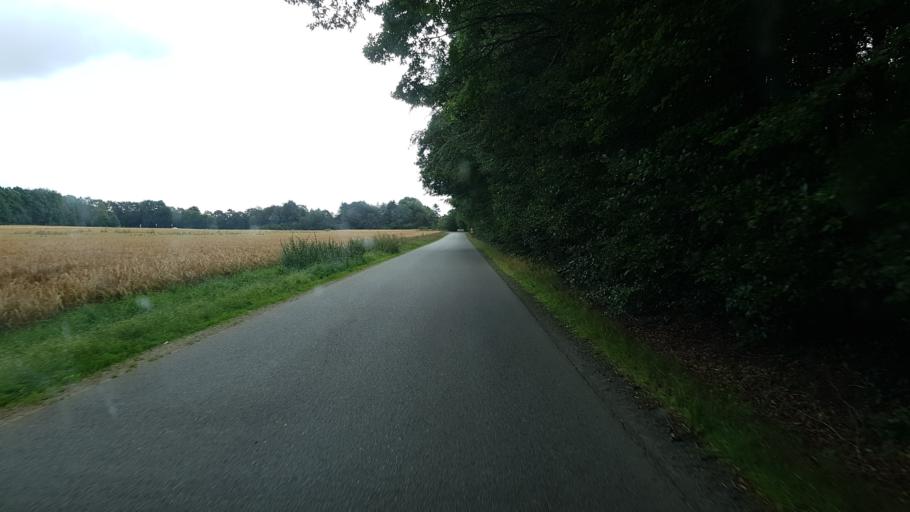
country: DK
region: South Denmark
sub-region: Vejen Kommune
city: Holsted
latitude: 55.6217
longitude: 8.8917
